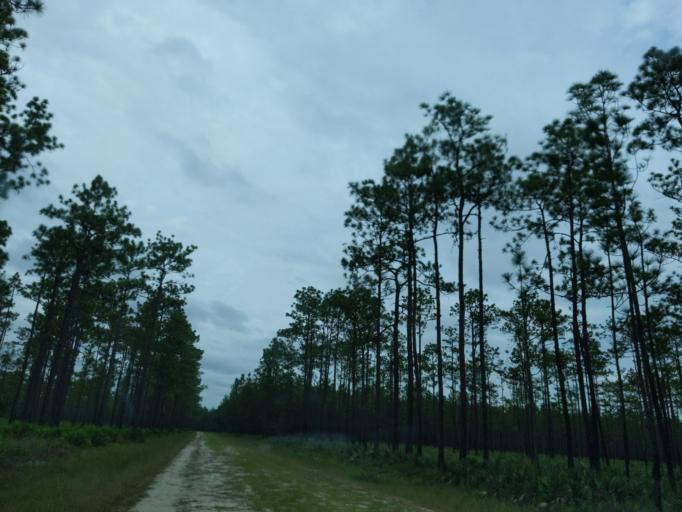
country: US
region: Florida
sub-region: Gadsden County
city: Midway
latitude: 30.3842
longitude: -84.4666
